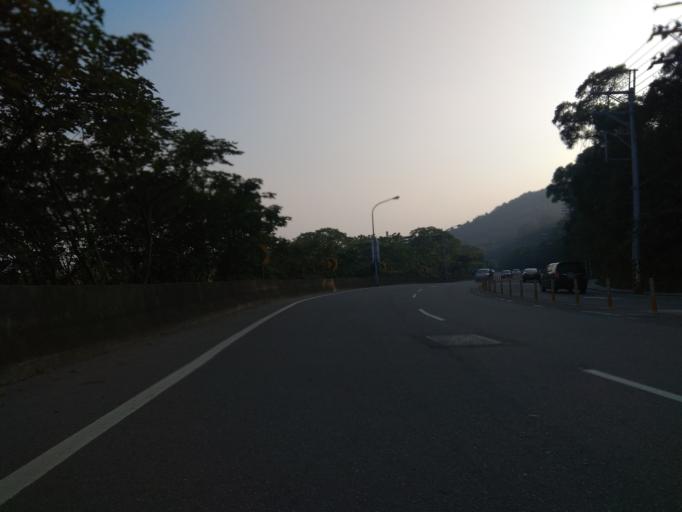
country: TW
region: Taiwan
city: Daxi
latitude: 24.9103
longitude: 121.1887
